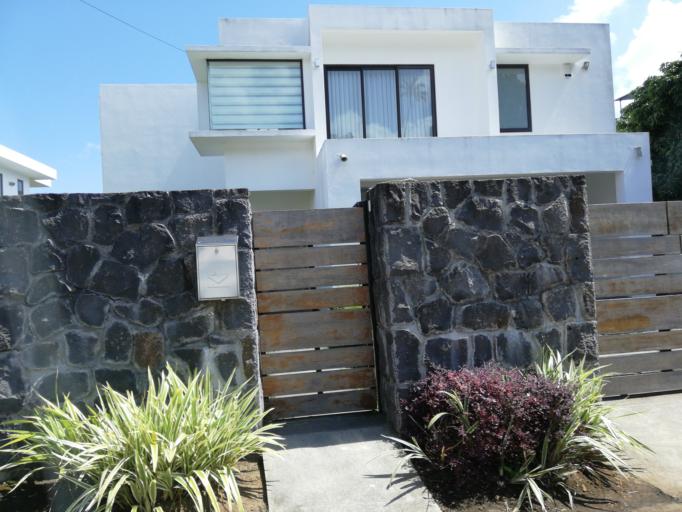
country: MU
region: Moka
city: Saint Pierre
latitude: -20.2257
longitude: 57.5279
